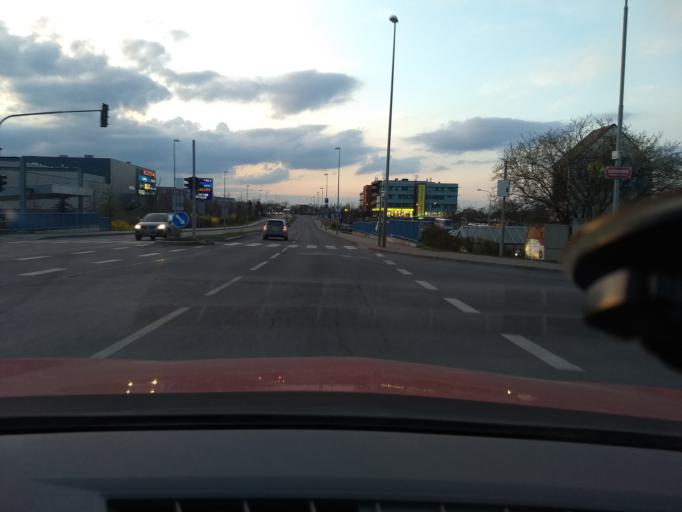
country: CZ
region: Central Bohemia
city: Hostivice
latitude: 50.0534
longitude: 14.2906
